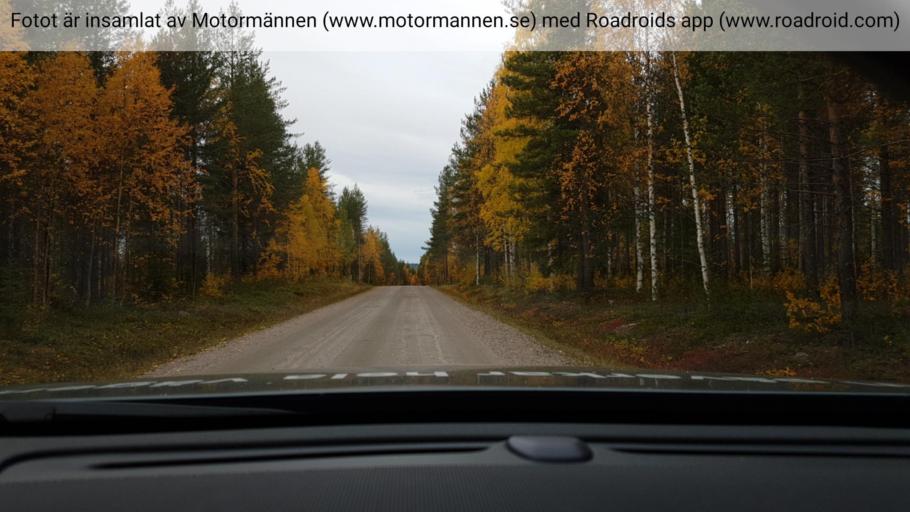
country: SE
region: Norrbotten
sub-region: Overkalix Kommun
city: OEverkalix
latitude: 66.2895
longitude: 22.9630
